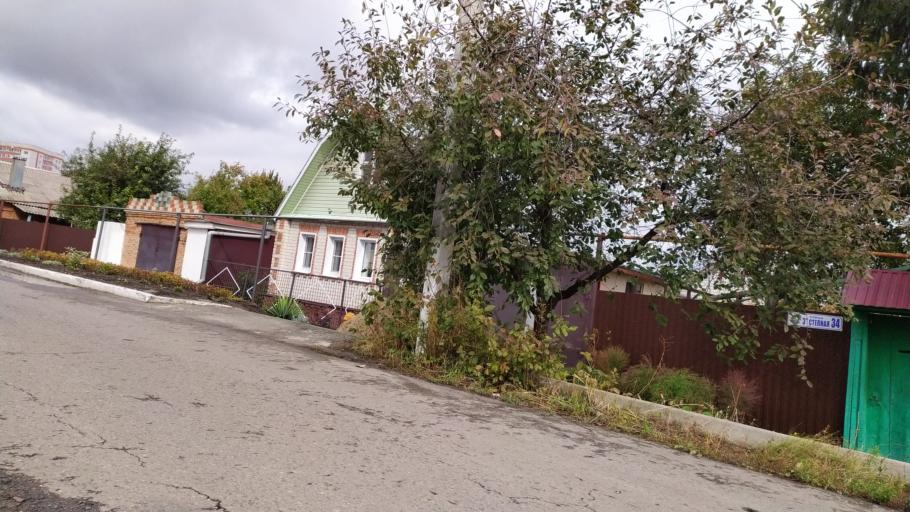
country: RU
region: Kursk
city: Kursk
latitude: 51.6449
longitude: 36.1474
